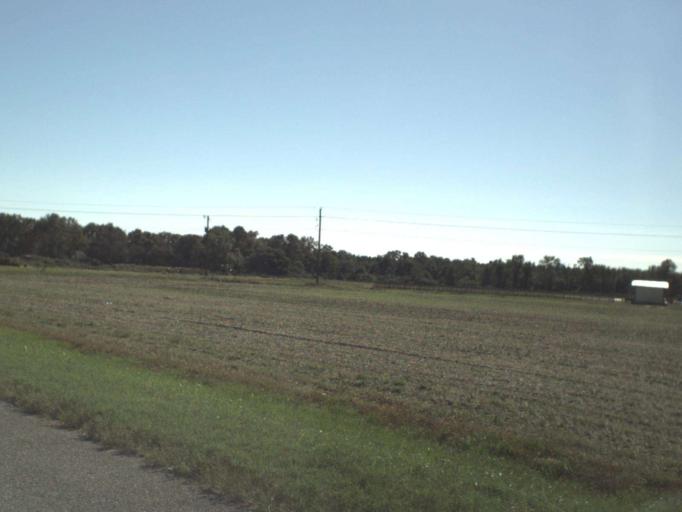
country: US
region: Florida
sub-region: Okaloosa County
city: Crestview
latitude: 30.8001
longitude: -86.7012
